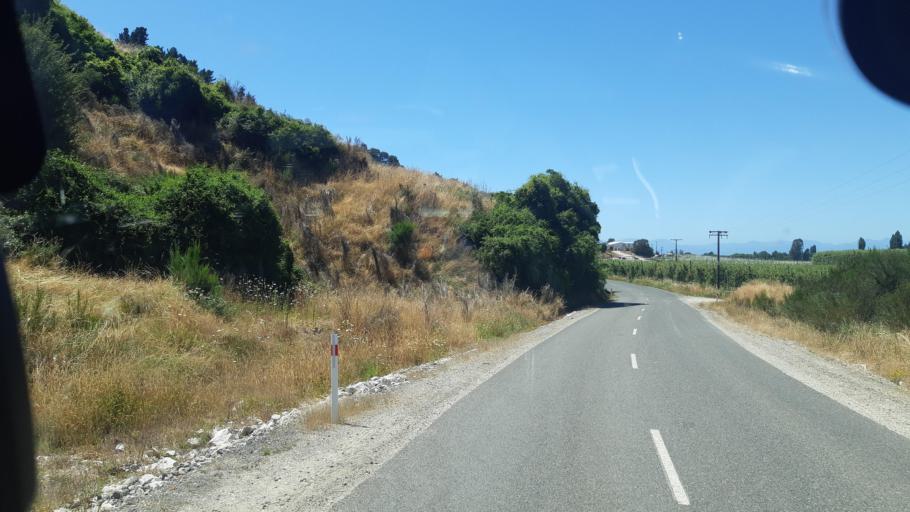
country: NZ
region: Tasman
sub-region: Tasman District
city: Motueka
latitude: -41.0525
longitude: 172.9582
